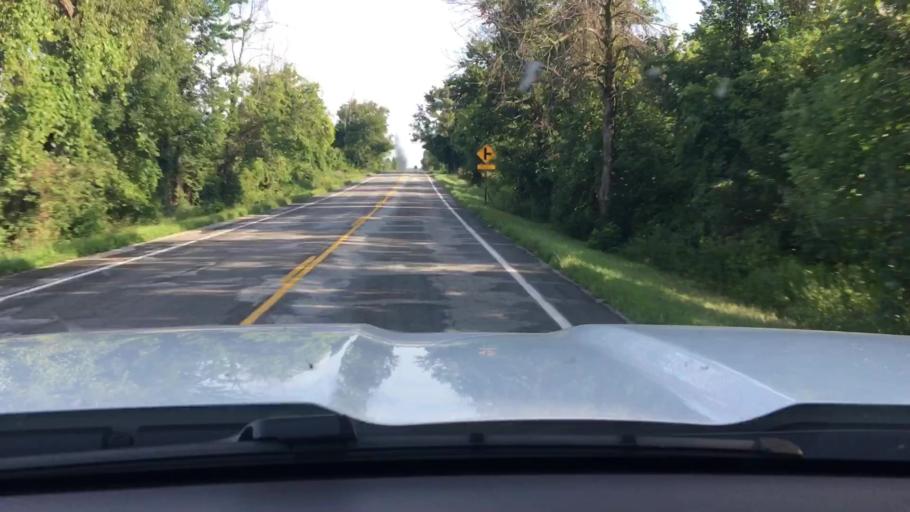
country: US
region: Michigan
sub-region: Kent County
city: Kent City
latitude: 43.2103
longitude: -85.7708
